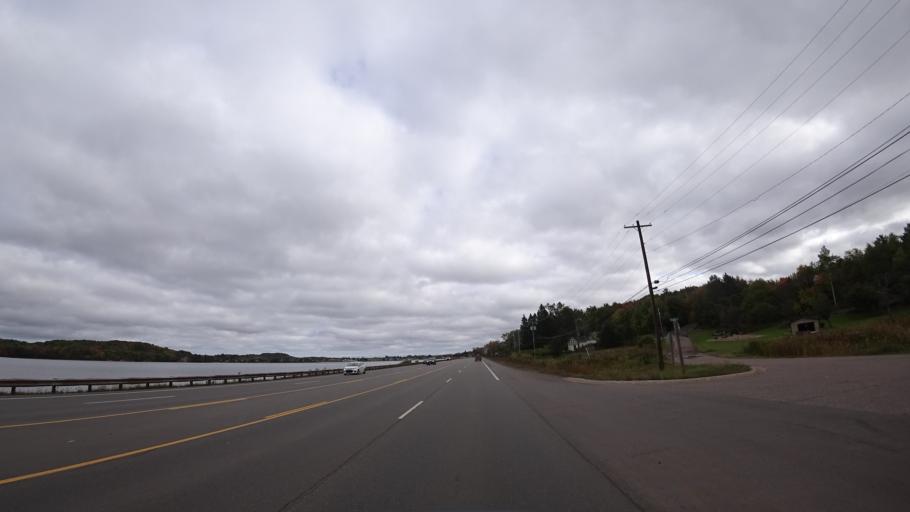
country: US
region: Michigan
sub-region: Marquette County
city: Negaunee
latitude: 46.5108
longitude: -87.6348
